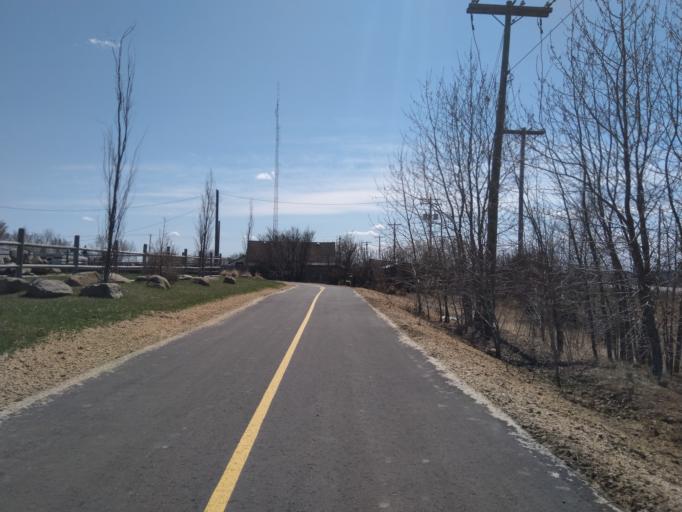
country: CA
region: Alberta
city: Chestermere
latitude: 50.9542
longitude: -113.9116
